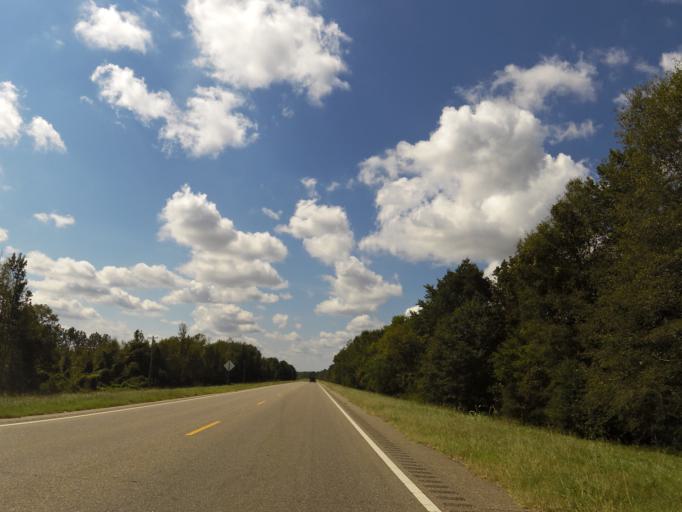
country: US
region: Alabama
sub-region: Dallas County
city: Selma
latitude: 32.3650
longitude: -87.1188
